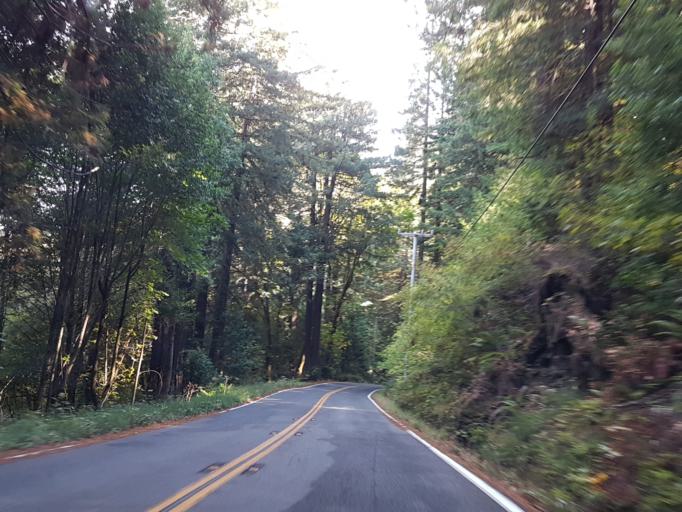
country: US
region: California
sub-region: Humboldt County
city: Rio Dell
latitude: 40.4191
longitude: -123.9777
